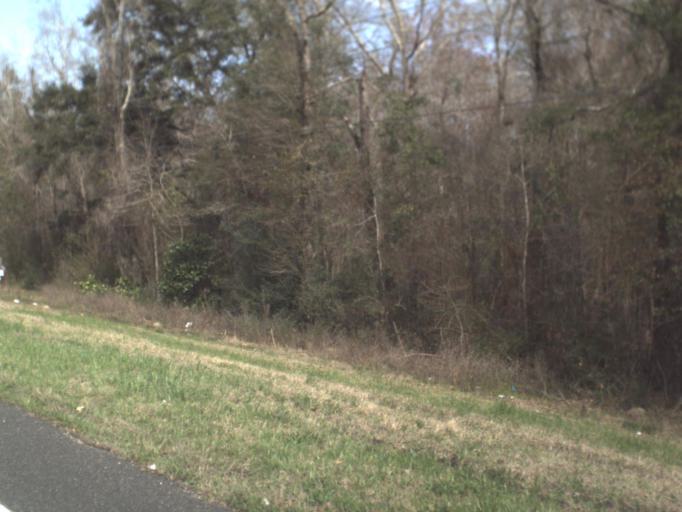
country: US
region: Florida
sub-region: Jackson County
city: Marianna
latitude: 30.7800
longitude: -85.3748
